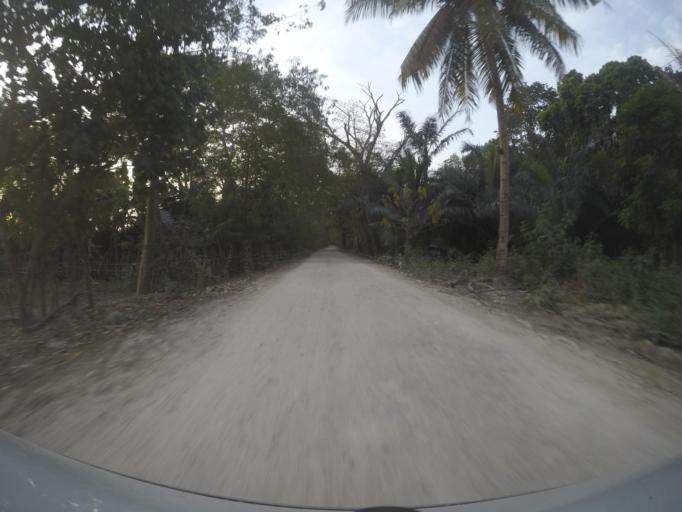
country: TL
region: Viqueque
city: Viqueque
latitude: -8.9364
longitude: 126.4138
